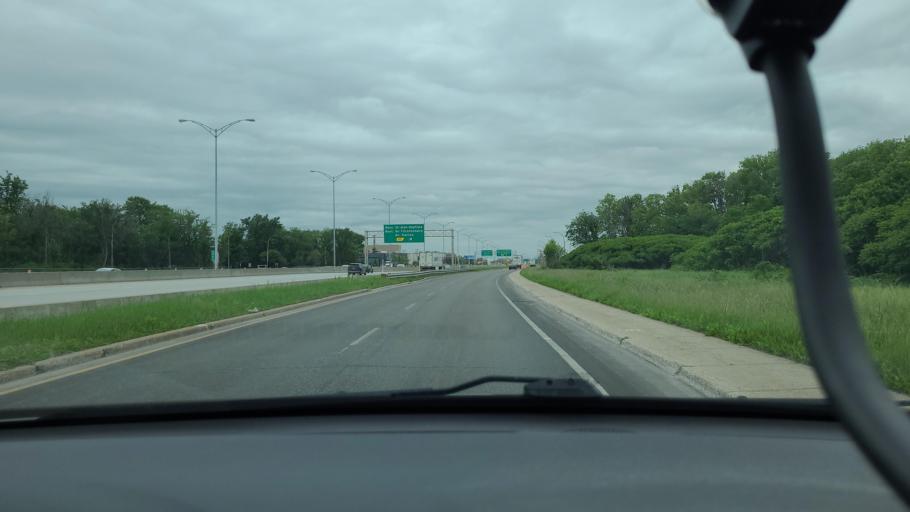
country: CA
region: Quebec
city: Montreal-Est
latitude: 45.6583
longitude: -73.5198
